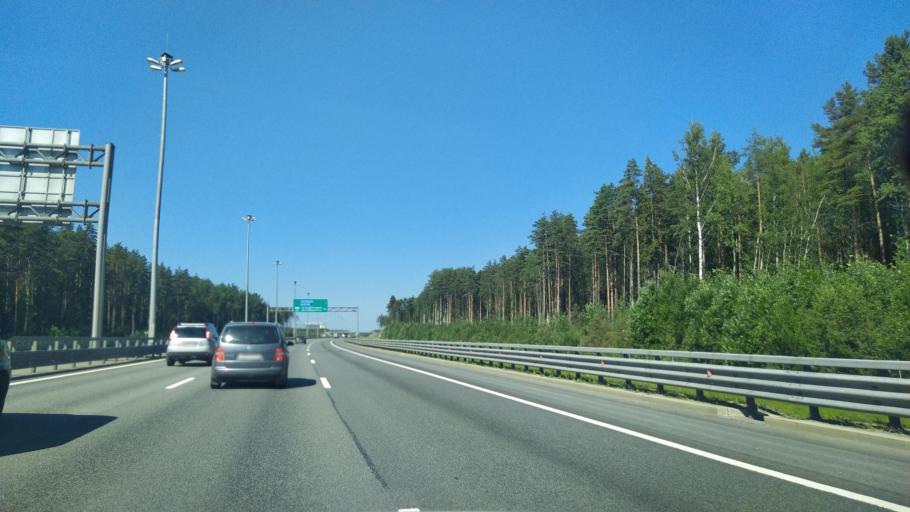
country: RU
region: Leningrad
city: Ol'gino
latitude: 59.8124
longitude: 29.9063
